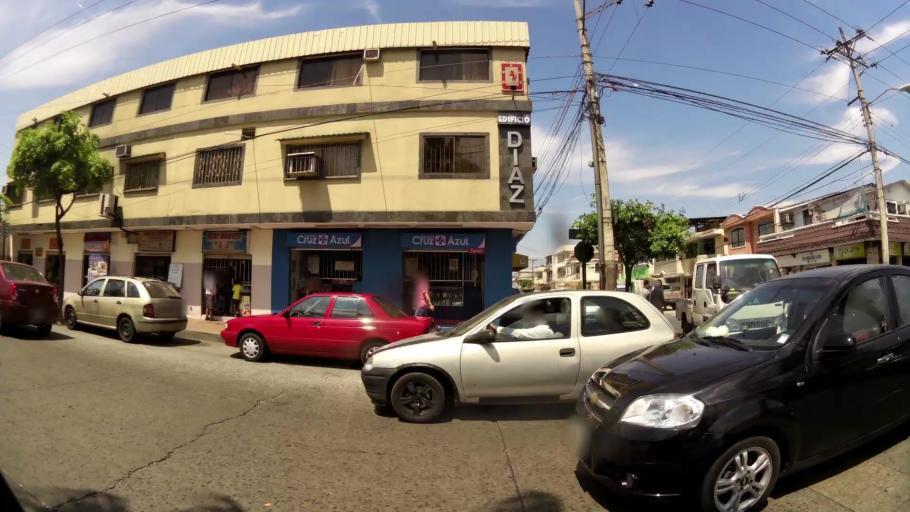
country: EC
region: Guayas
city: Eloy Alfaro
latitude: -2.1390
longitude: -79.9065
